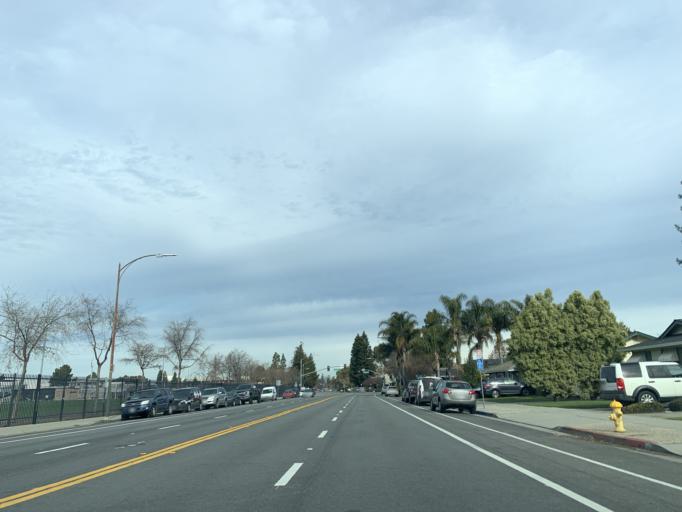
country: US
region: California
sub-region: Santa Clara County
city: Buena Vista
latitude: 37.3119
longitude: -121.9233
